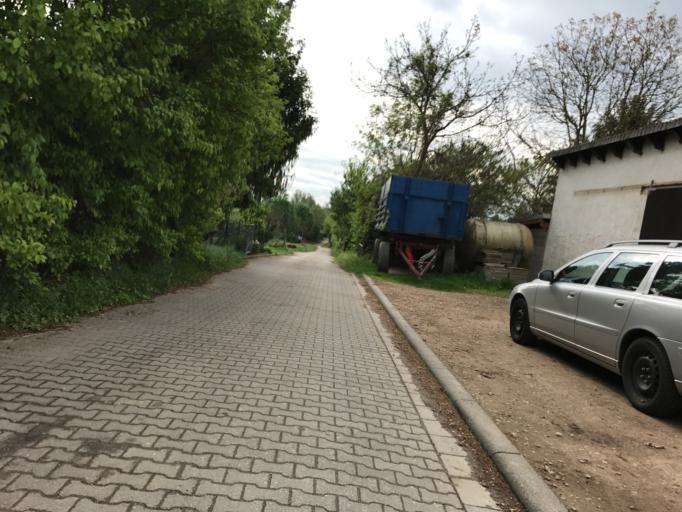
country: DE
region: Rheinland-Pfalz
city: Jugenheim
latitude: 49.8943
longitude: 8.0892
